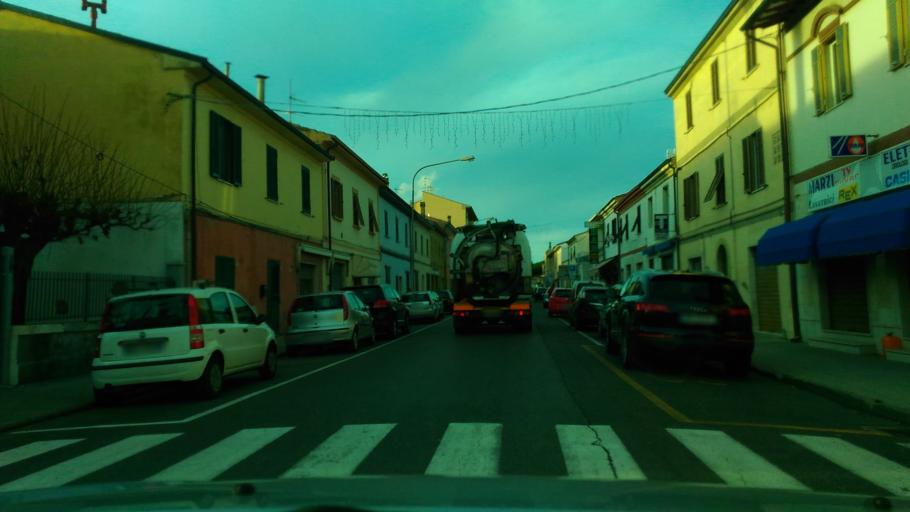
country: IT
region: Tuscany
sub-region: Provincia di Livorno
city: S.P. in Palazzi
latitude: 43.3253
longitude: 10.5086
